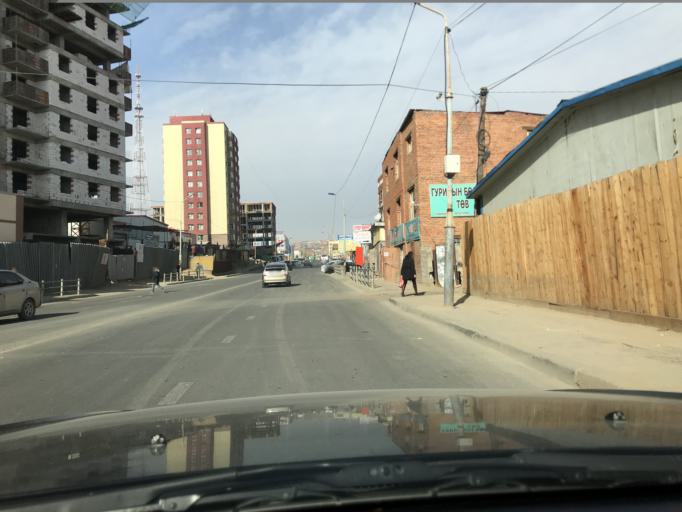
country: MN
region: Ulaanbaatar
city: Ulaanbaatar
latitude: 47.9257
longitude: 106.8954
